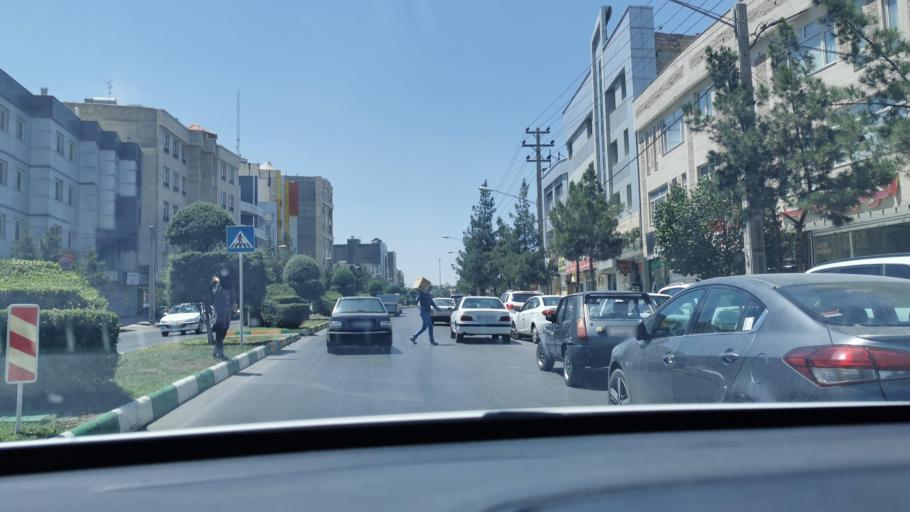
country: IR
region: Razavi Khorasan
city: Mashhad
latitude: 36.3382
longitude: 59.4868
